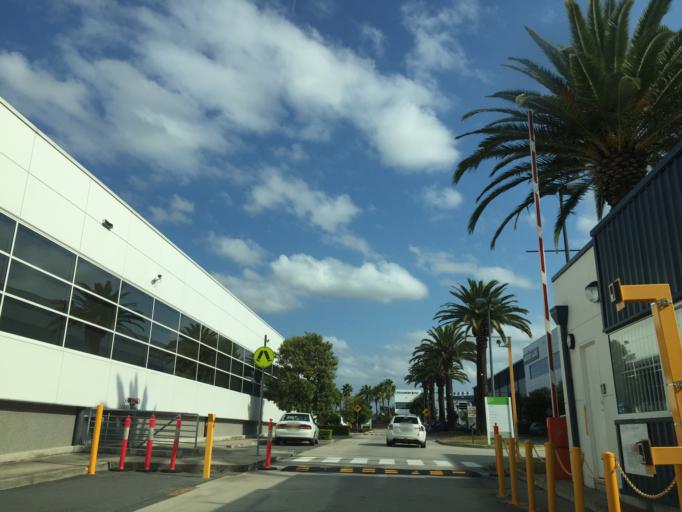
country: AU
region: New South Wales
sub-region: Strathfield
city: Homebush
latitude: -33.8575
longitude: 151.0649
